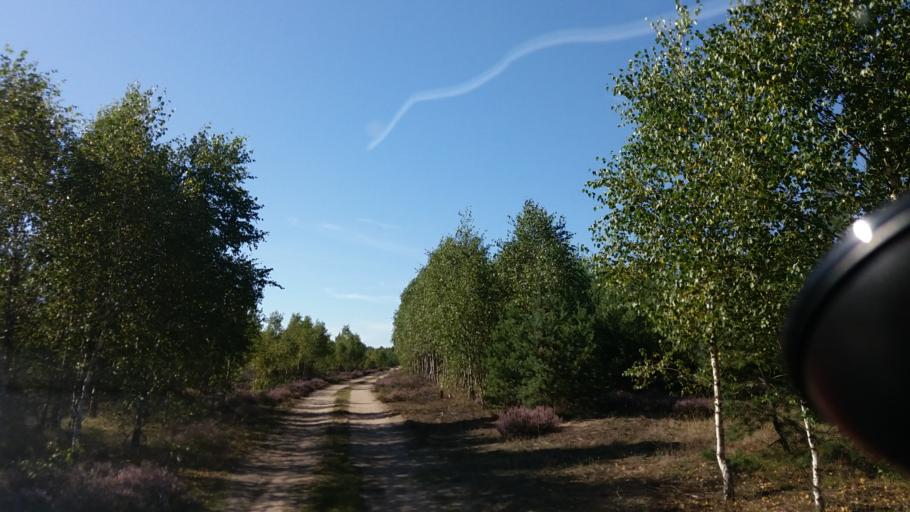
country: PL
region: West Pomeranian Voivodeship
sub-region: Powiat szczecinecki
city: Borne Sulinowo
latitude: 53.5692
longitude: 16.5181
